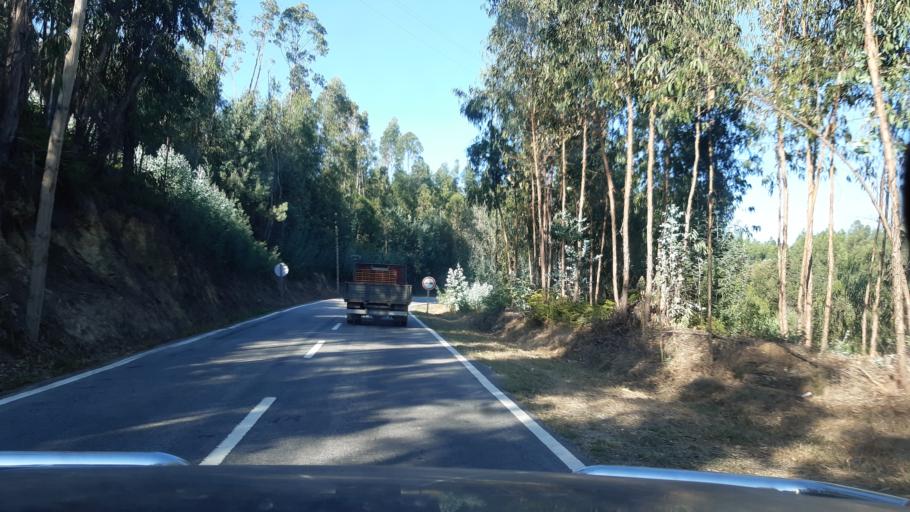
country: PT
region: Aveiro
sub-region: Agueda
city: Aguada de Cima
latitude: 40.5645
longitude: -8.3890
